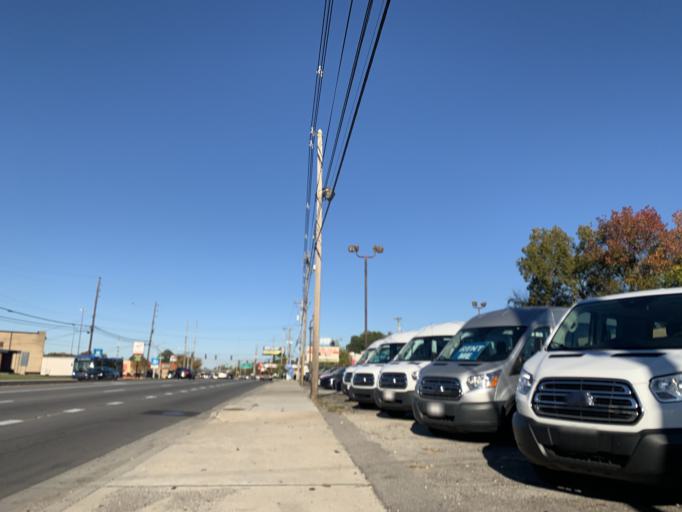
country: US
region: Kentucky
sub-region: Jefferson County
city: Shively
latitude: 38.1795
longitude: -85.8173
